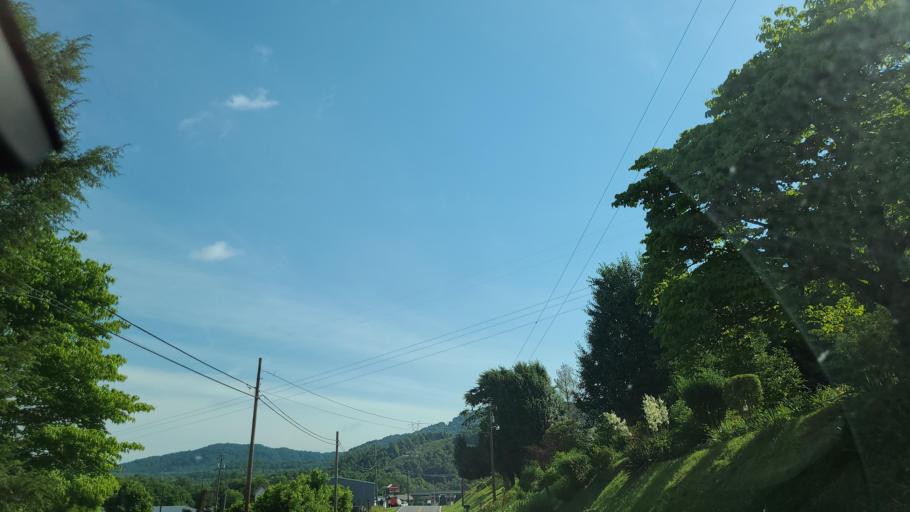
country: US
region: Kentucky
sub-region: Bell County
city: Pineville
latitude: 36.7877
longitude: -83.7569
